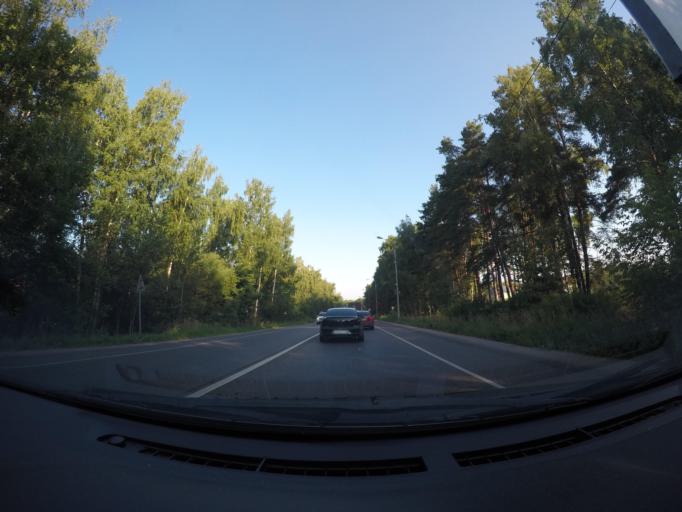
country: RU
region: Moskovskaya
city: Il'inskiy
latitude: 55.6505
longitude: 38.1278
